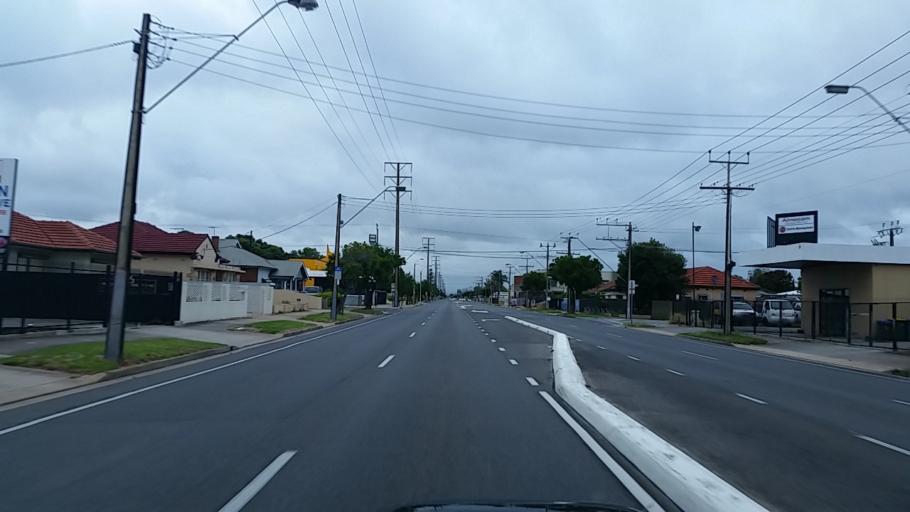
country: AU
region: South Australia
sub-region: Charles Sturt
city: Royal Park
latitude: -34.8752
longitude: 138.5125
